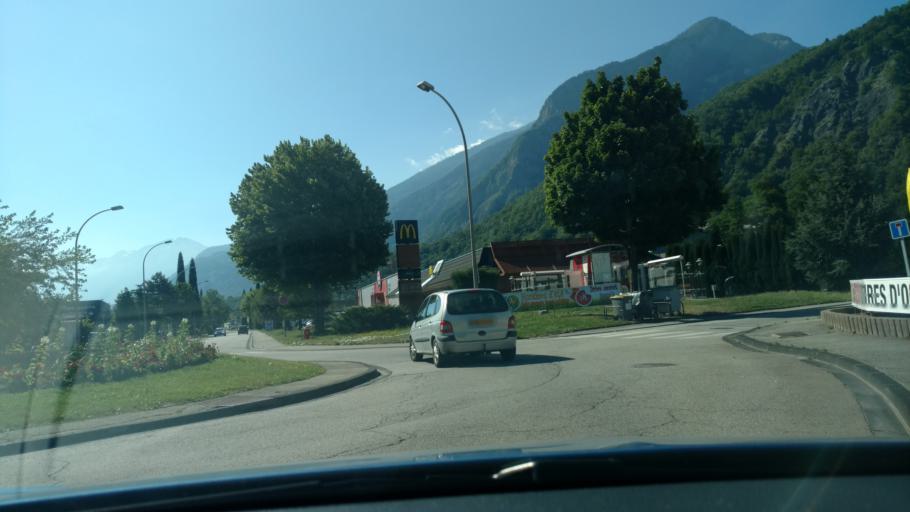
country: FR
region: Rhone-Alpes
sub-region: Departement de la Savoie
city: Villargondran
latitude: 45.2708
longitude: 6.3641
